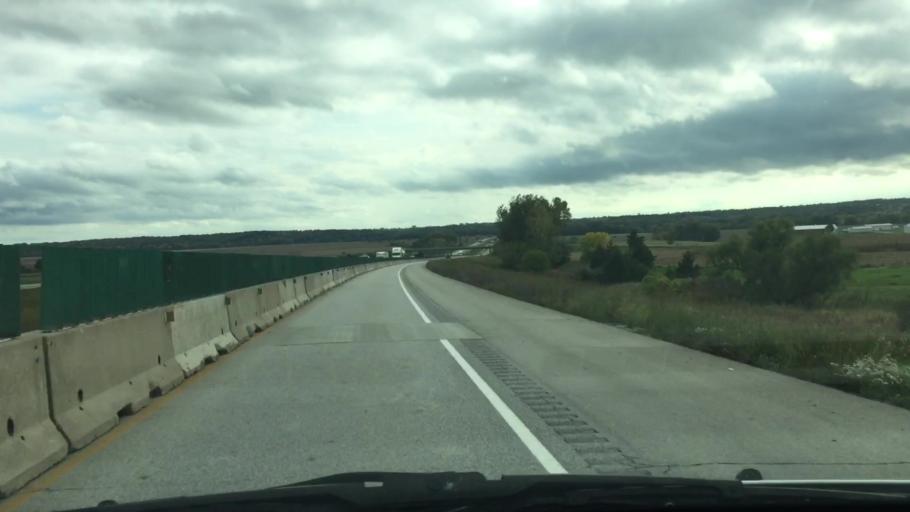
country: US
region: Iowa
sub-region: Decatur County
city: Lamoni
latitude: 40.6875
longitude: -93.8464
